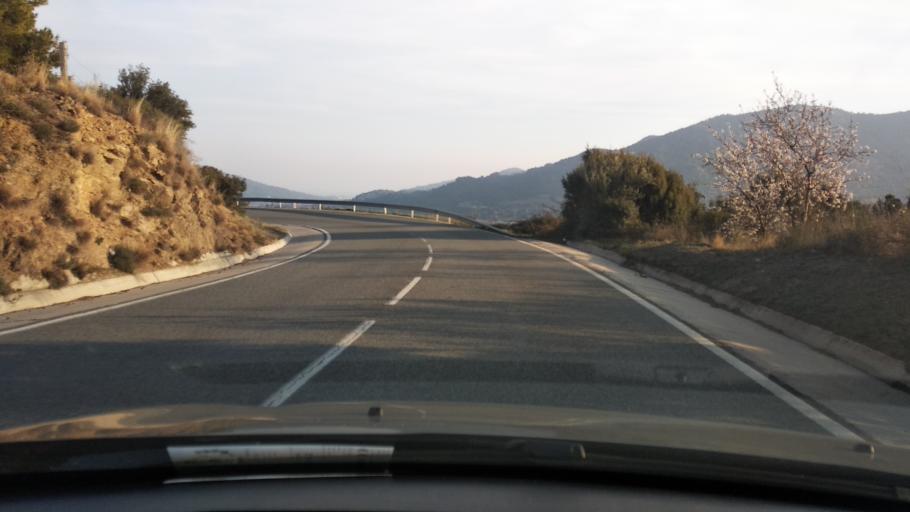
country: ES
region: Catalonia
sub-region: Provincia de Tarragona
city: Alforja
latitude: 41.2171
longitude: 0.9643
